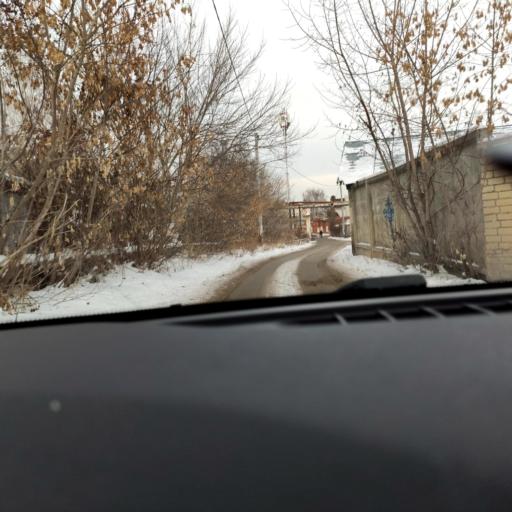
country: RU
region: Samara
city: Samara
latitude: 53.2555
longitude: 50.1837
